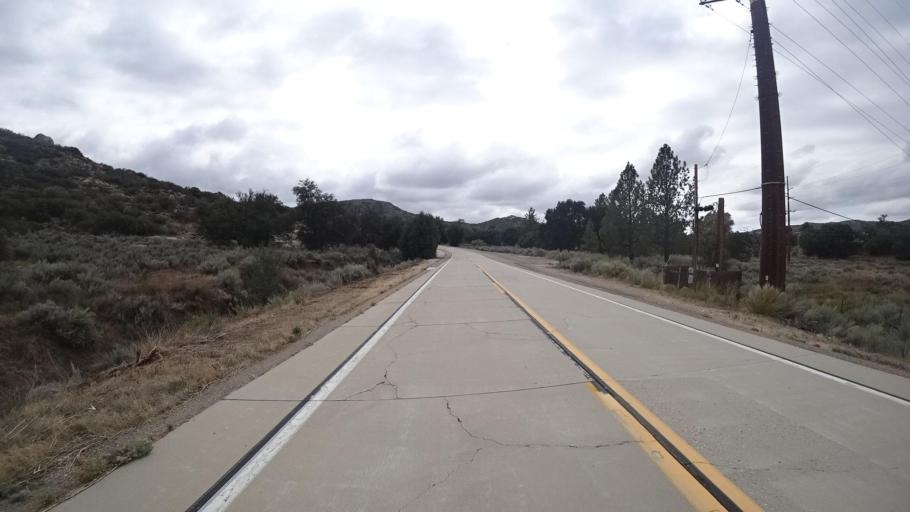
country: US
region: California
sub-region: San Diego County
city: Pine Valley
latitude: 32.7329
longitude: -116.4831
